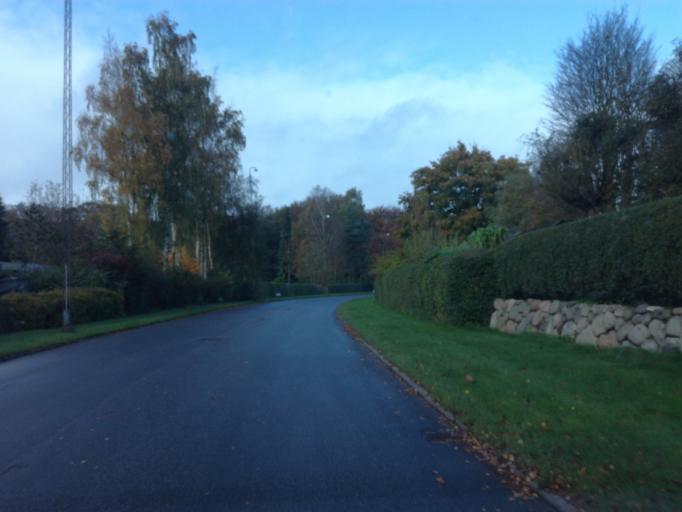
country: DK
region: South Denmark
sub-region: Vejle Kommune
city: Vejle
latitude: 55.6779
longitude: 9.5473
